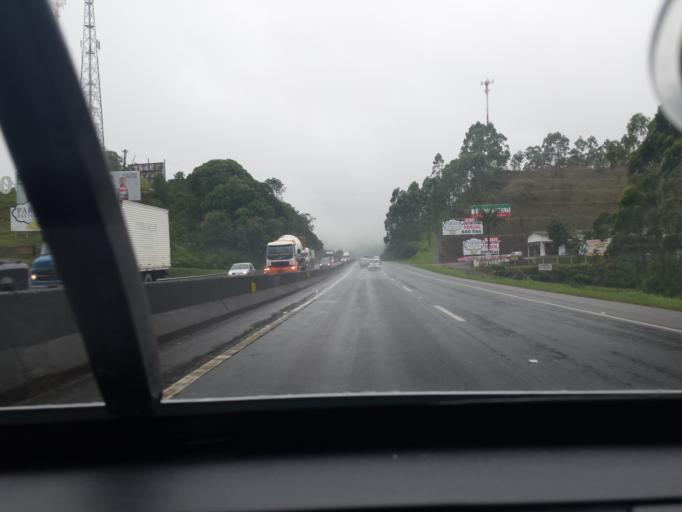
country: BR
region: Santa Catarina
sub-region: Balneario Camboriu
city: Balneario Camboriu
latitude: -26.9747
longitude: -48.6826
